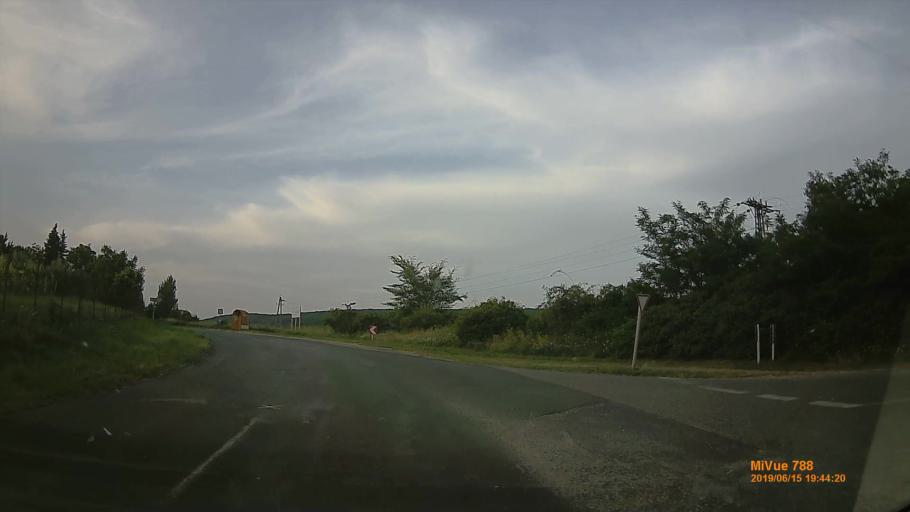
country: HU
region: Veszprem
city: Csopak
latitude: 46.9982
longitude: 17.9651
